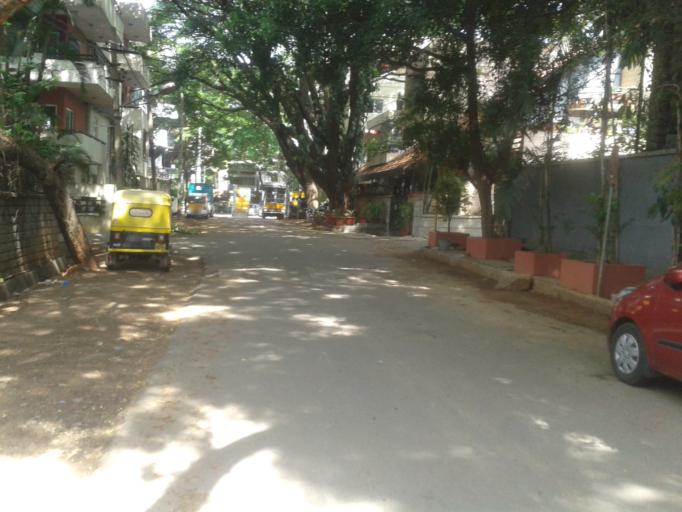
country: IN
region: Karnataka
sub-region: Bangalore Urban
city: Bangalore
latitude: 12.9756
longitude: 77.6419
